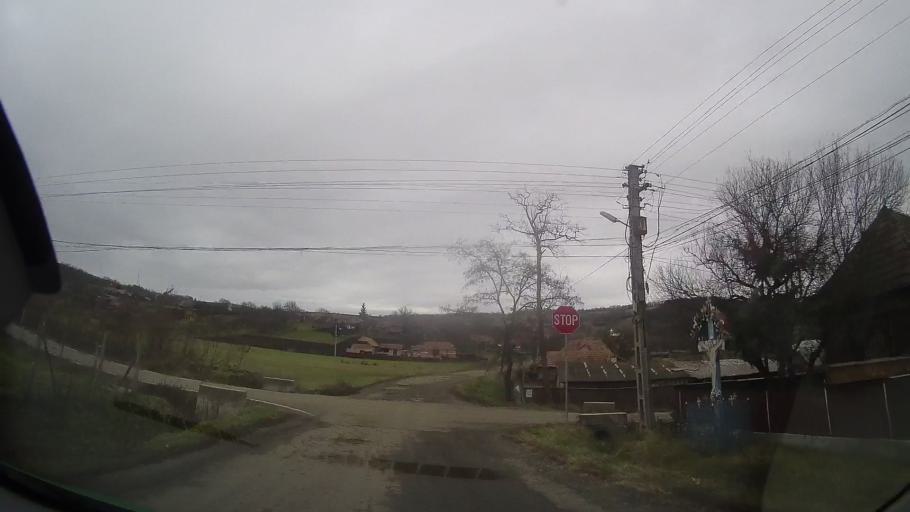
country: RO
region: Mures
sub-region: Comuna Bala
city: Bala
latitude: 46.7081
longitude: 24.5014
